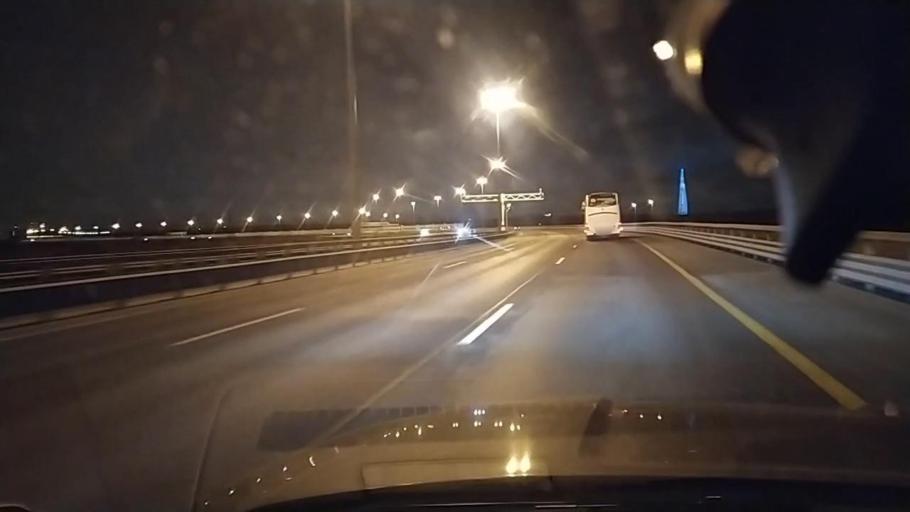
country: RU
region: St.-Petersburg
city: Lakhtinskiy
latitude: 60.0442
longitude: 30.1522
